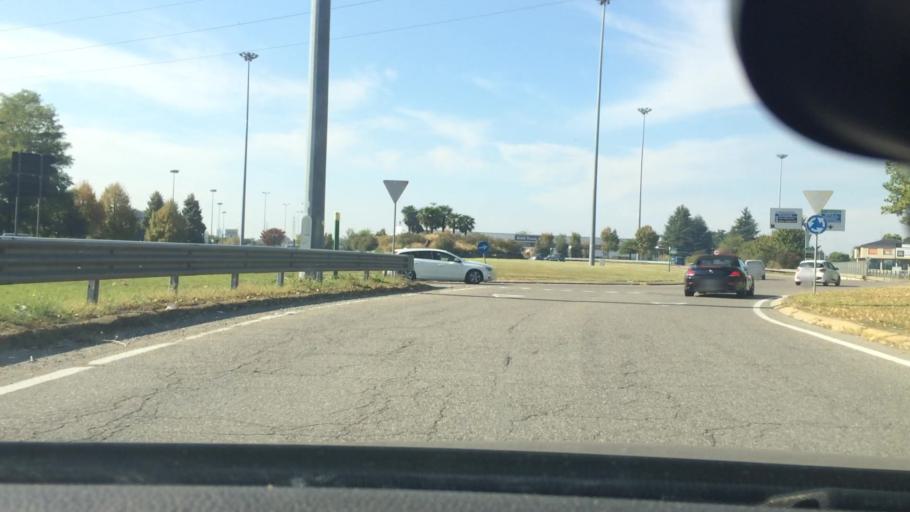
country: IT
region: Lombardy
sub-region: Citta metropolitana di Milano
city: Rescaldina
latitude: 45.6124
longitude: 8.9661
